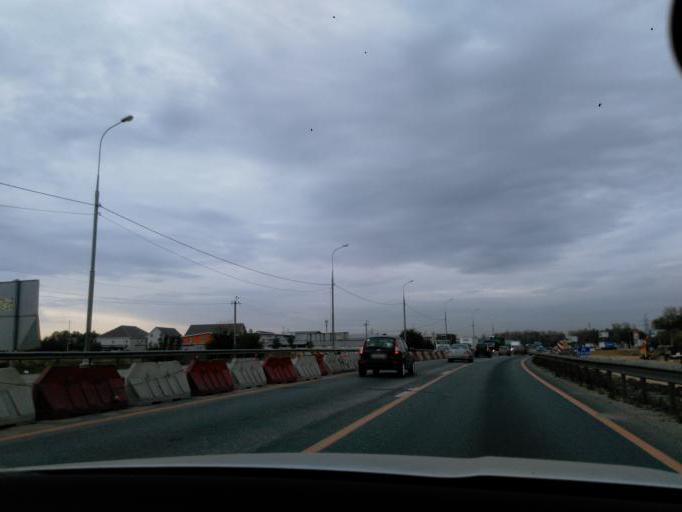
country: RU
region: Moscow
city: Severnyy
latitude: 55.9653
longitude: 37.5339
